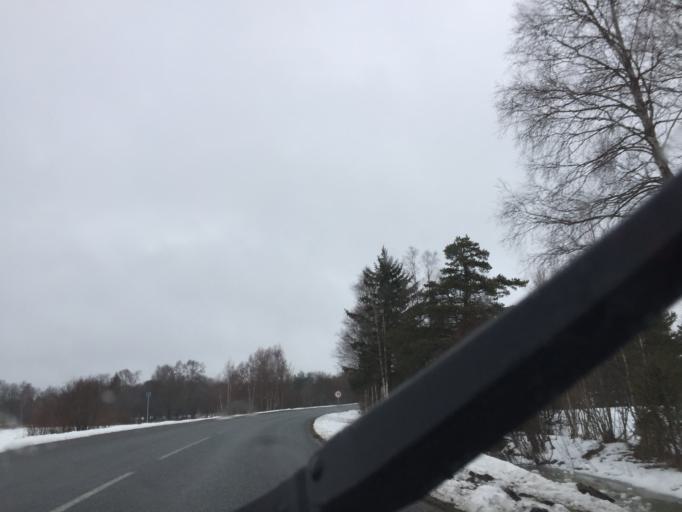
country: EE
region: Saare
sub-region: Kuressaare linn
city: Kuressaare
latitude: 58.3536
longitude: 22.0330
